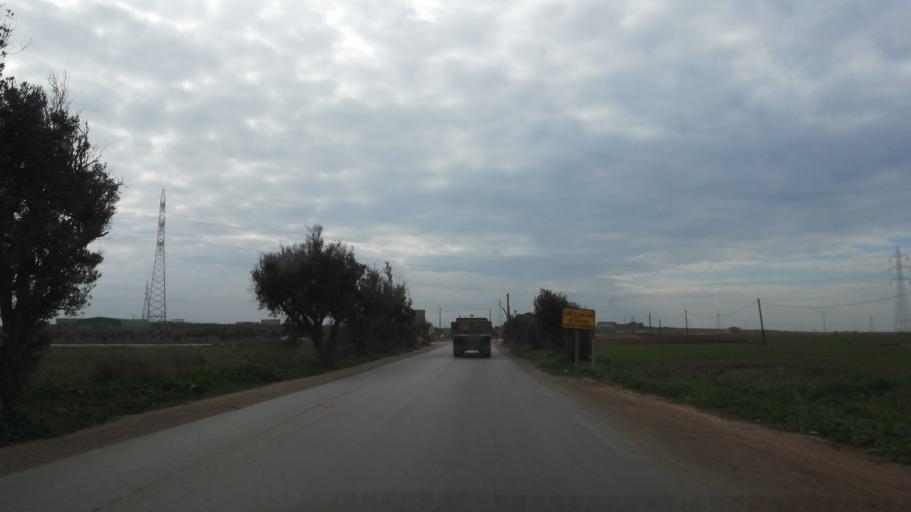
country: DZ
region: Oran
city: Ain el Bya
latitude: 35.7923
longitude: -0.3417
